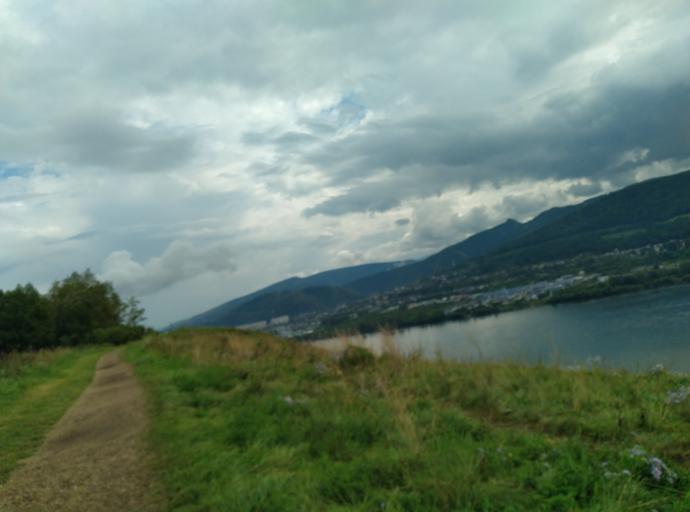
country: RU
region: Krasnoyarskiy
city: Krasnoyarsk
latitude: 55.9831
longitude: 92.7483
